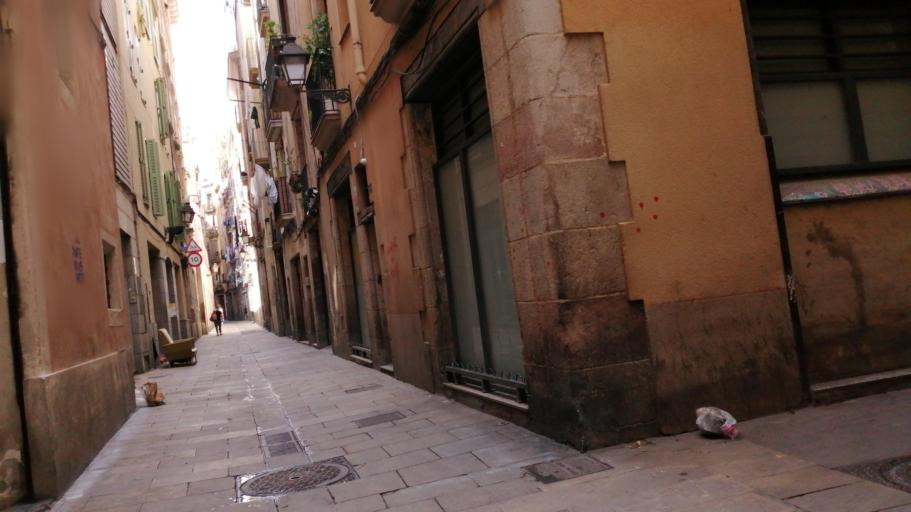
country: ES
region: Catalonia
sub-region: Provincia de Barcelona
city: Ciutat Vella
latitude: 41.3879
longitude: 2.1775
